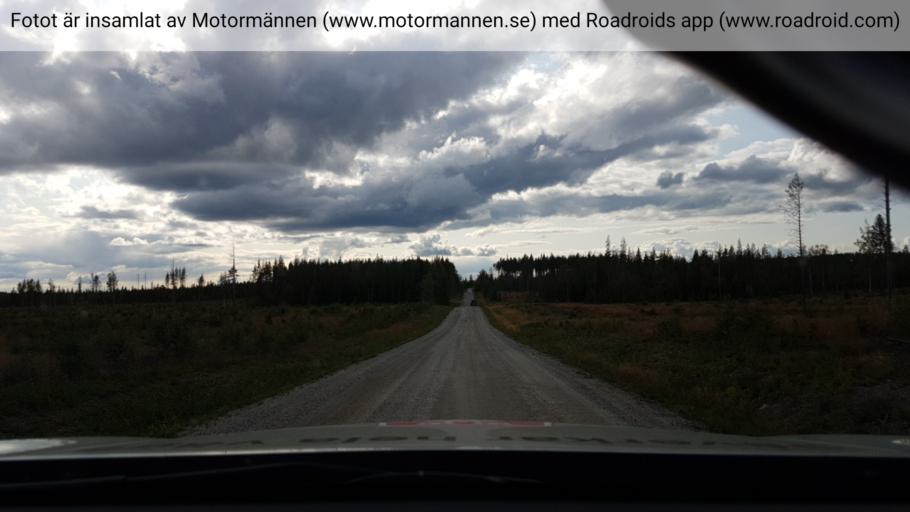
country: SE
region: Vaesterbotten
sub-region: Lycksele Kommun
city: Lycksele
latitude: 64.6787
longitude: 18.7146
